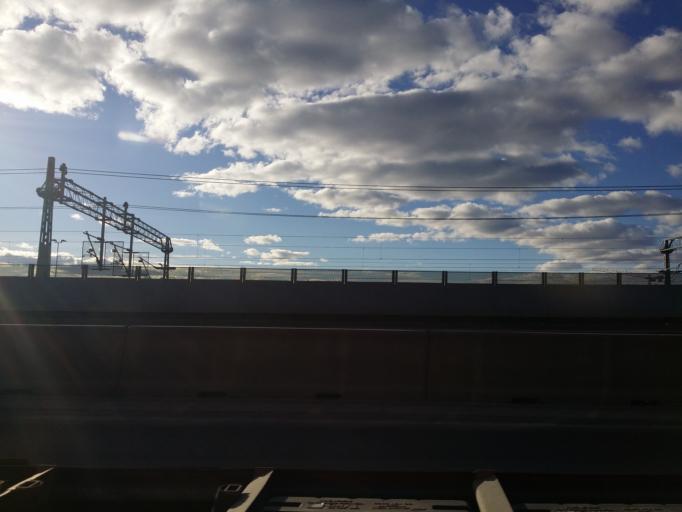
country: NO
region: Oslo
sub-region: Oslo
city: Oslo
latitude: 59.8986
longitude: 10.7563
